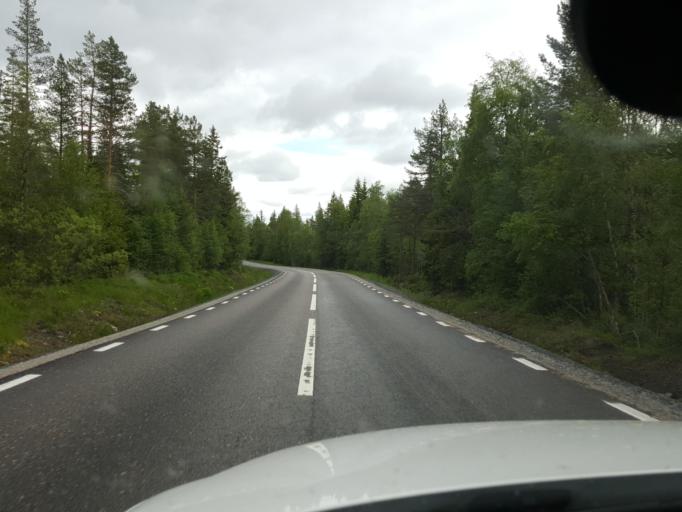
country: SE
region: Gaevleborg
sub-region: Ljusdals Kommun
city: Farila
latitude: 61.7563
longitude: 15.4225
